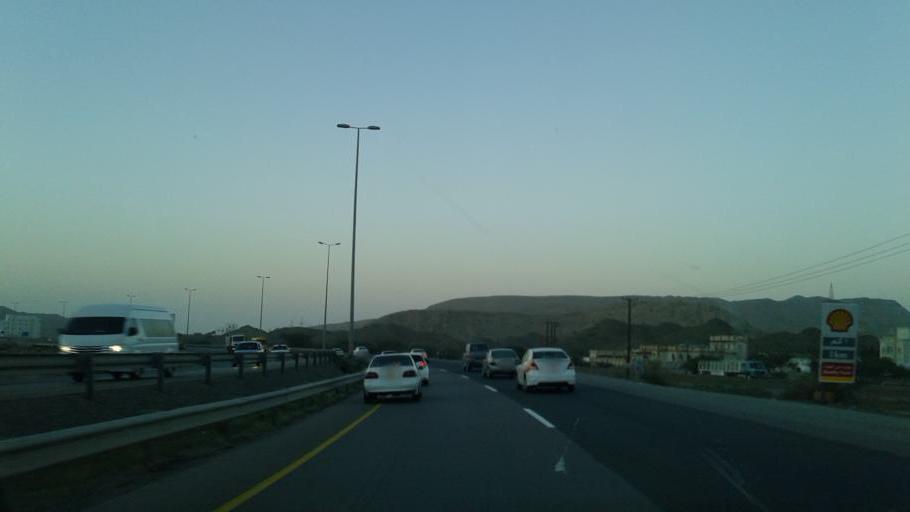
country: OM
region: Muhafazat ad Dakhiliyah
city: Bidbid
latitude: 23.5175
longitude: 58.1923
